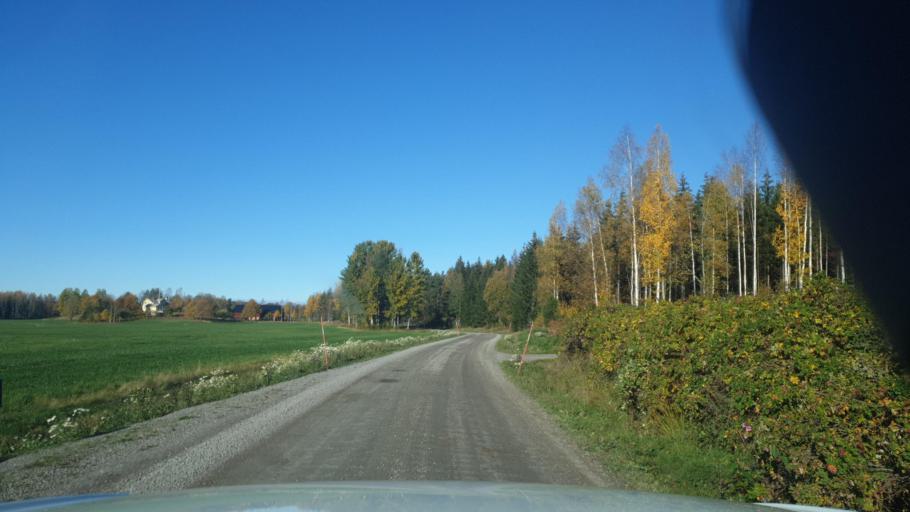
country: SE
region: Vaermland
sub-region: Arvika Kommun
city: Arvika
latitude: 59.4929
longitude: 12.7378
